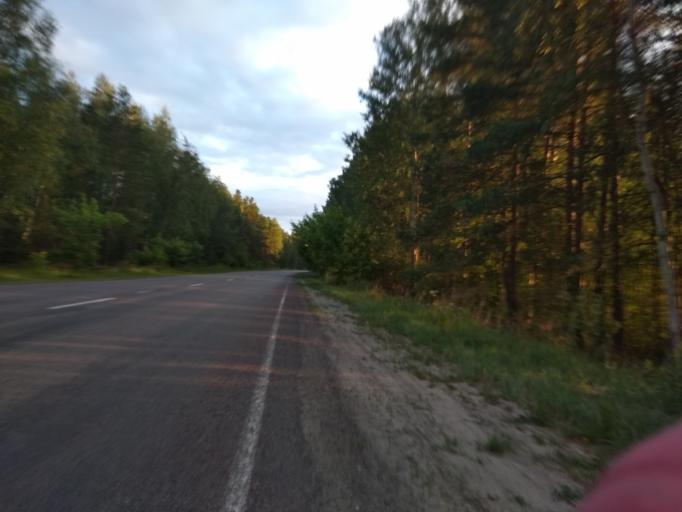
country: RU
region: Moskovskaya
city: Kerva
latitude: 55.5829
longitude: 39.6950
